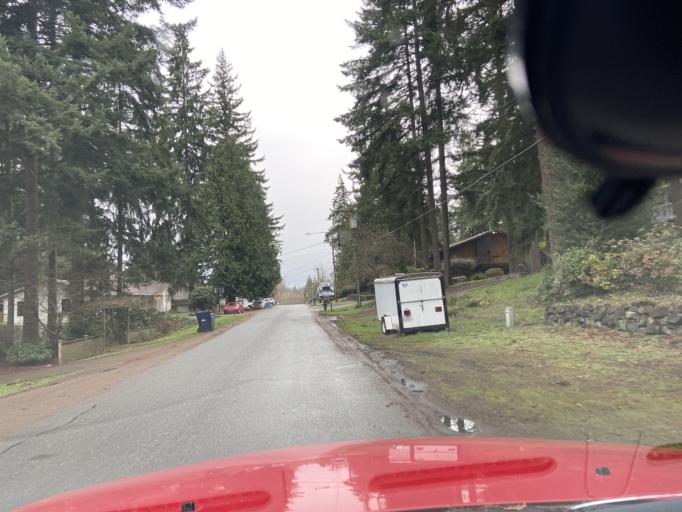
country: US
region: Washington
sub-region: Snohomish County
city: Fobes Hill
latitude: 47.9648
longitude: -122.1005
